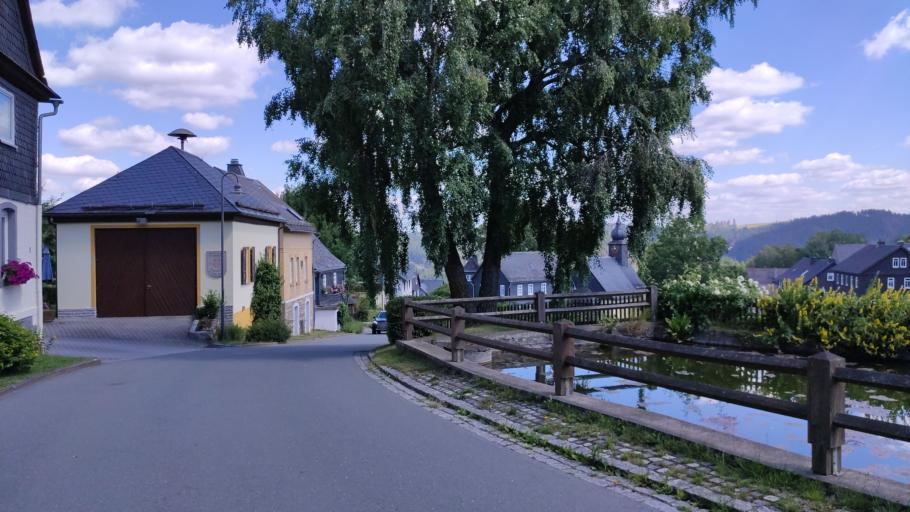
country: DE
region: Bavaria
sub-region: Upper Franconia
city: Ludwigsstadt
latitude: 50.5070
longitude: 11.4179
